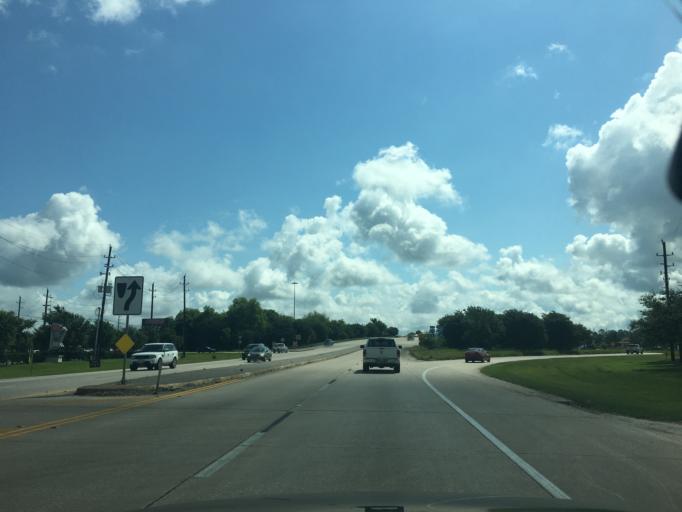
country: US
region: Texas
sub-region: Harris County
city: Spring
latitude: 30.0650
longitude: -95.4382
